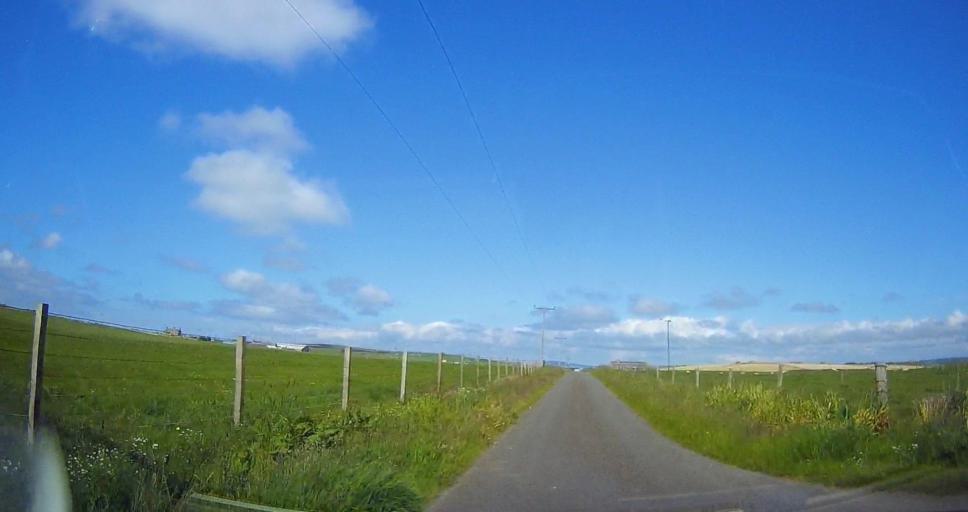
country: GB
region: Scotland
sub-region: Orkney Islands
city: Kirkwall
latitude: 58.8294
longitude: -2.8970
